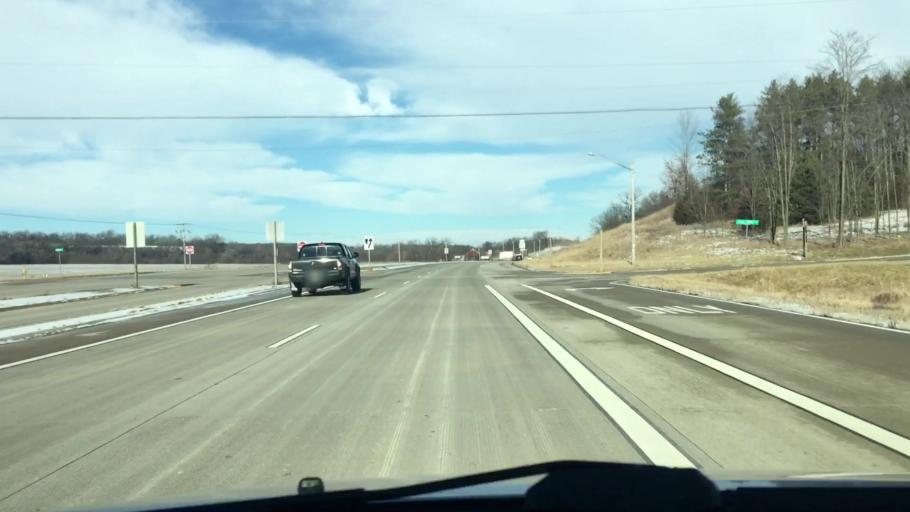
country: US
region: Wisconsin
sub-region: Waukesha County
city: Mukwonago
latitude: 42.9004
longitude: -88.3449
